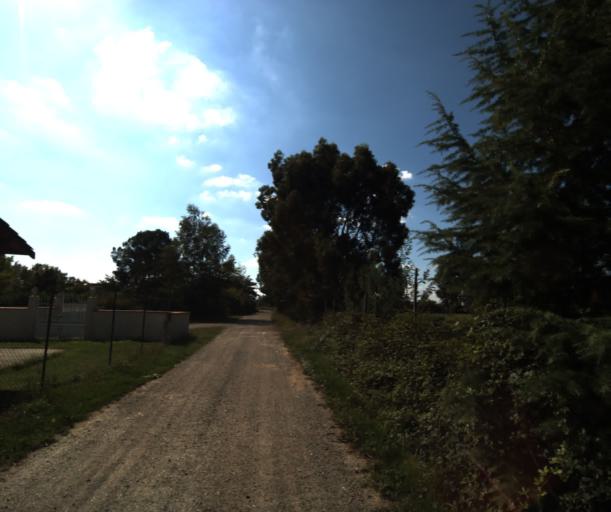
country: FR
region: Midi-Pyrenees
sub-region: Departement de la Haute-Garonne
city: Fonsorbes
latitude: 43.5023
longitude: 1.2168
